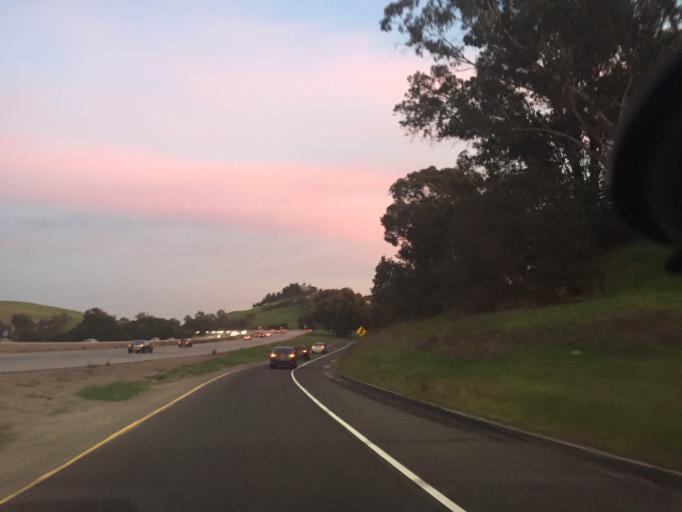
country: US
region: California
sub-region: Santa Clara County
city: Los Altos Hills
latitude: 37.3913
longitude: -122.1669
